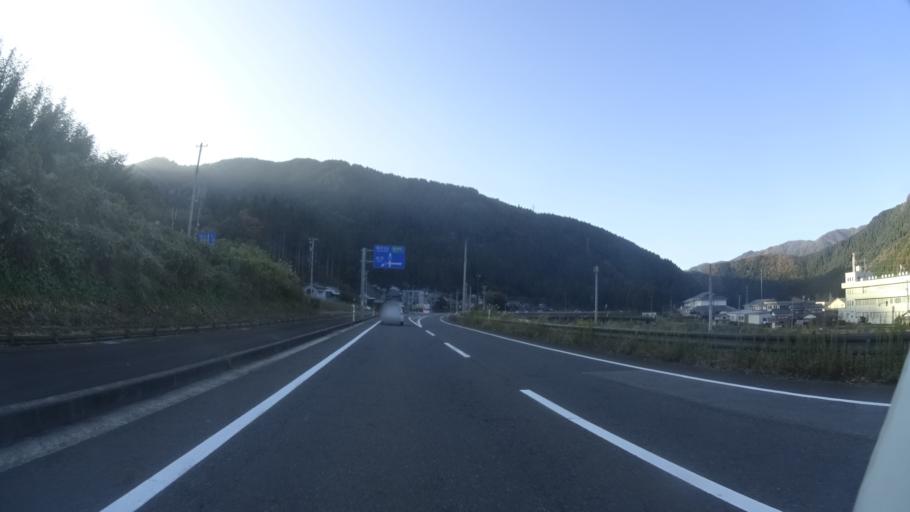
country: JP
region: Fukui
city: Ono
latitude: 35.9971
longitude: 136.3606
